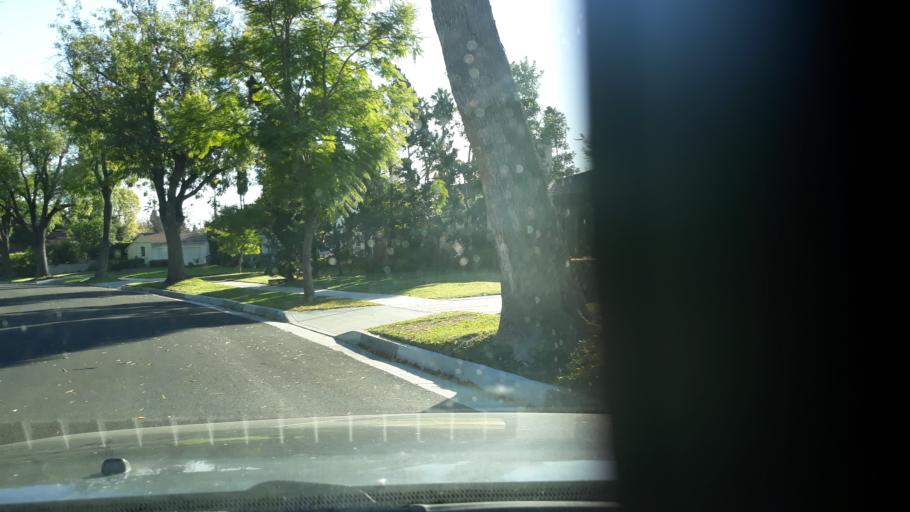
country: US
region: California
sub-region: Los Angeles County
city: San Marino
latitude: 34.1225
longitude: -118.0942
